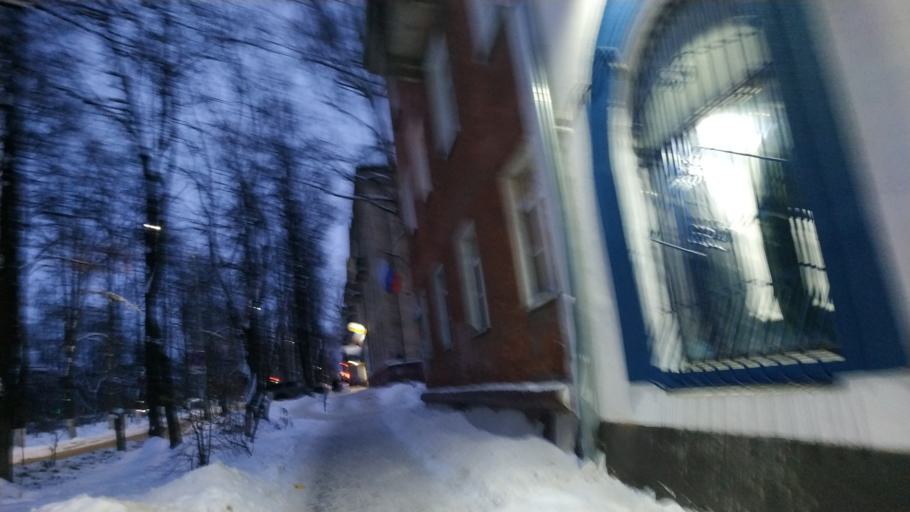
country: RU
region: Moskovskaya
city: Shchelkovo
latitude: 55.9224
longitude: 37.9768
